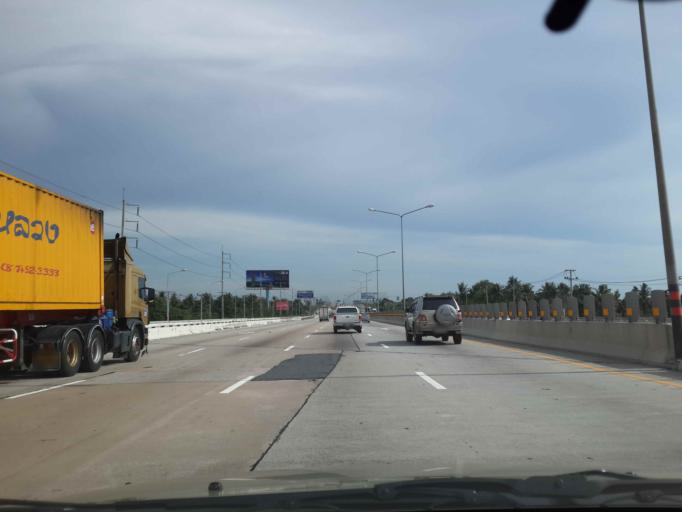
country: TH
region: Chon Buri
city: Si Racha
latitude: 13.1870
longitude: 100.9974
